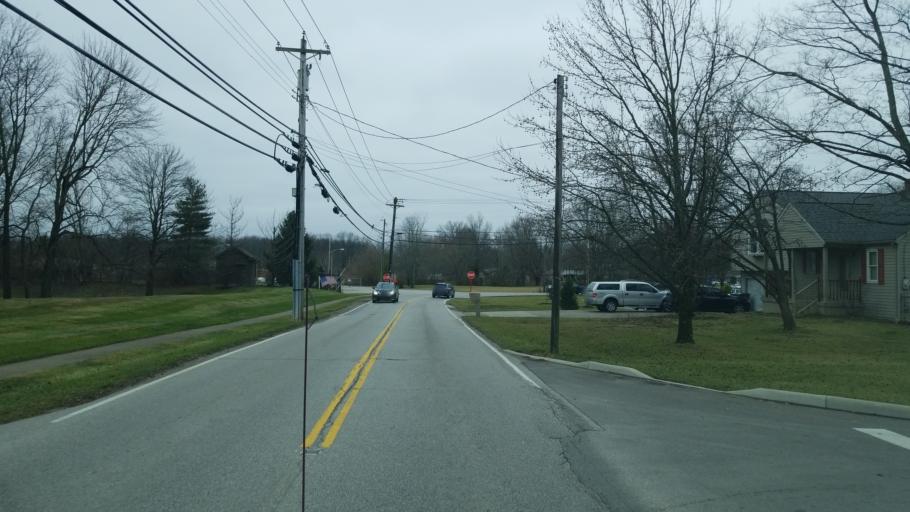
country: US
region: Ohio
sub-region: Clermont County
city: Summerside
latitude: 39.0893
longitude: -84.2642
